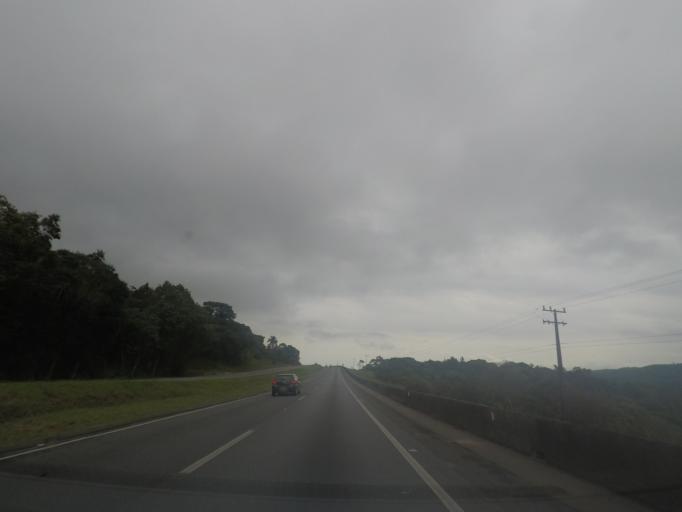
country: BR
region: Parana
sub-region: Campina Grande Do Sul
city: Campina Grande do Sul
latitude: -25.1451
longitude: -48.8580
